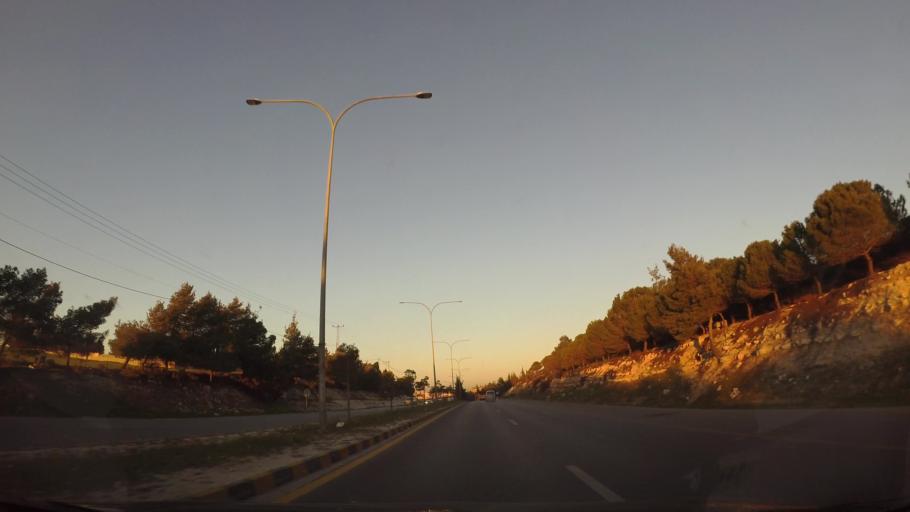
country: JO
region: Amman
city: Umm as Summaq
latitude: 31.8670
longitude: 35.8305
